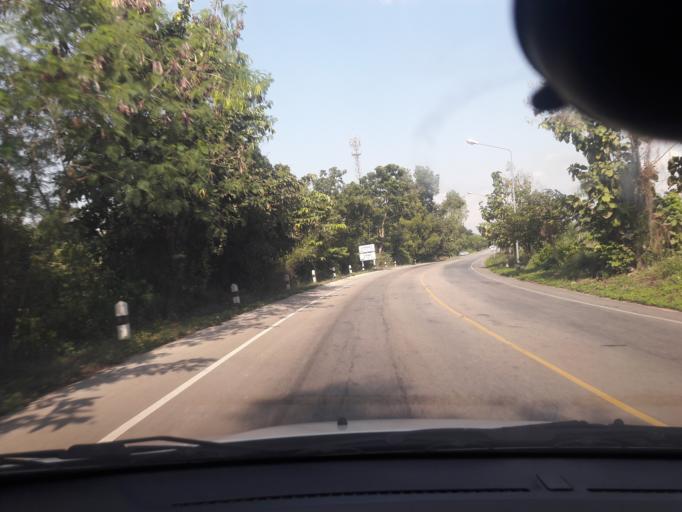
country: TH
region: Lampang
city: Mae Tha
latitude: 18.2107
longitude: 99.4943
